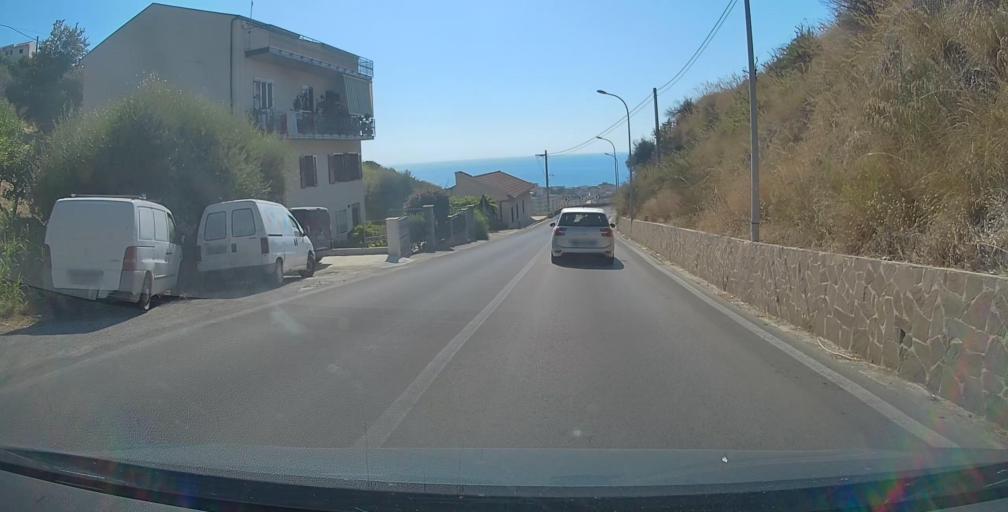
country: IT
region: Sicily
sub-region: Messina
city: Capo d'Orlando
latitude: 38.1570
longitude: 14.7508
